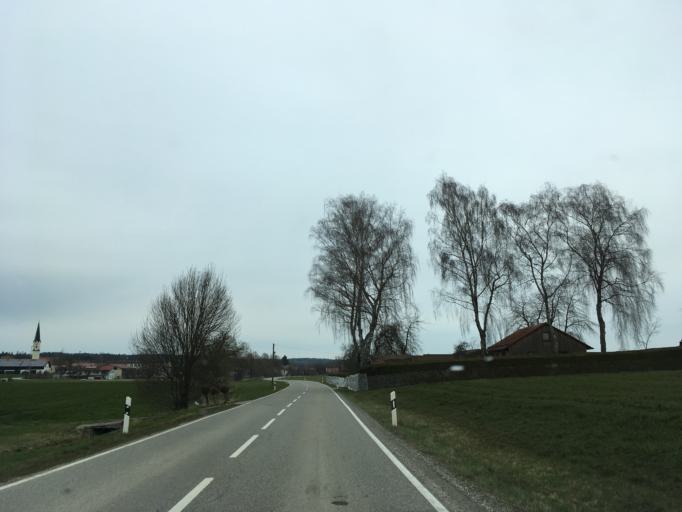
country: DE
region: Bavaria
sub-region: Upper Bavaria
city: Schnaitsee
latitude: 48.1003
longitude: 12.4081
